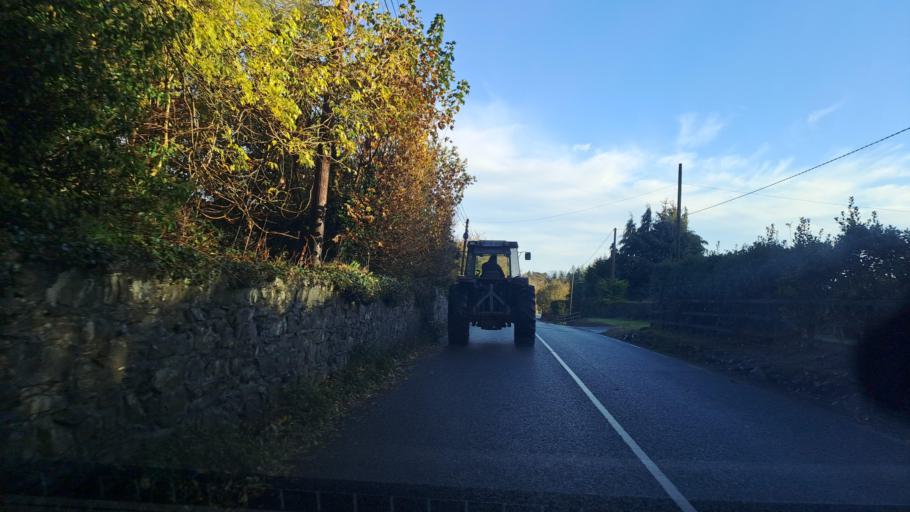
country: IE
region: Ulster
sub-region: County Monaghan
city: Monaghan
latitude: 54.2186
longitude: -6.9821
